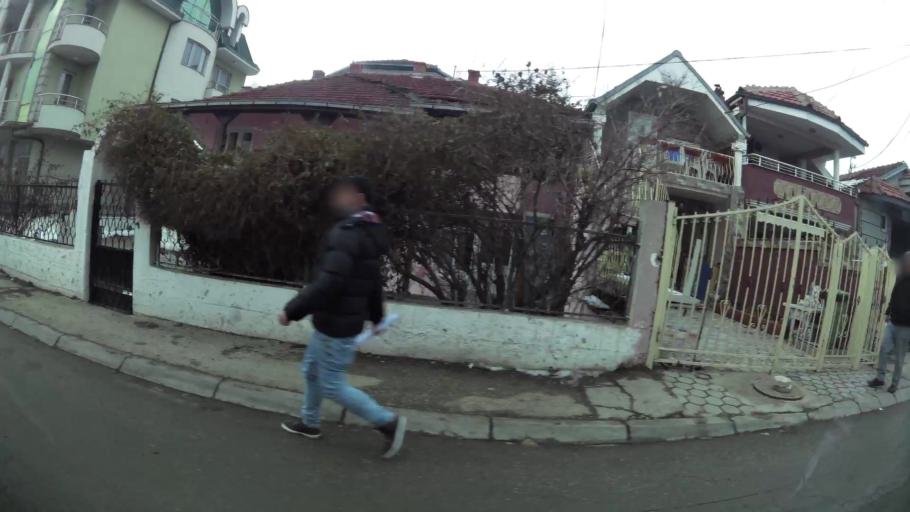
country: MK
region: Suto Orizari
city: Suto Orizare
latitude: 42.0424
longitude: 21.4226
